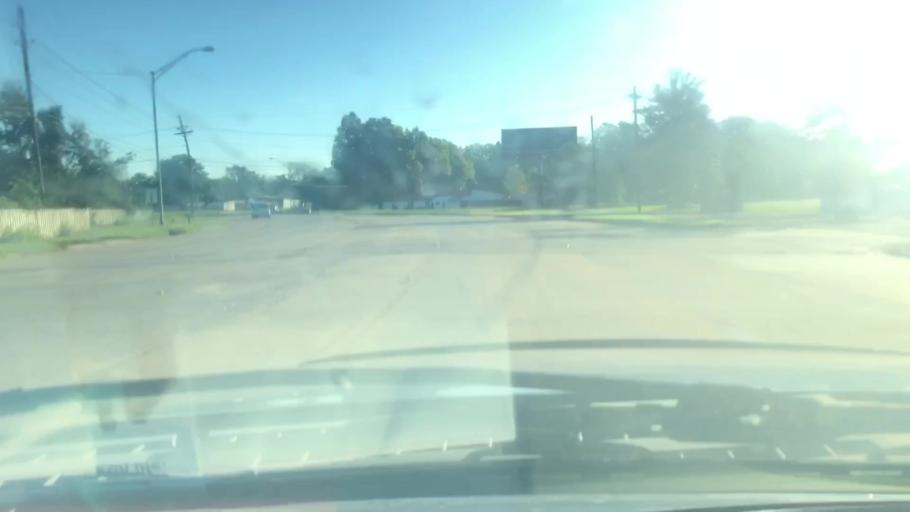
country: US
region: Texas
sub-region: Bowie County
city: Texarkana
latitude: 33.4218
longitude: -94.0728
